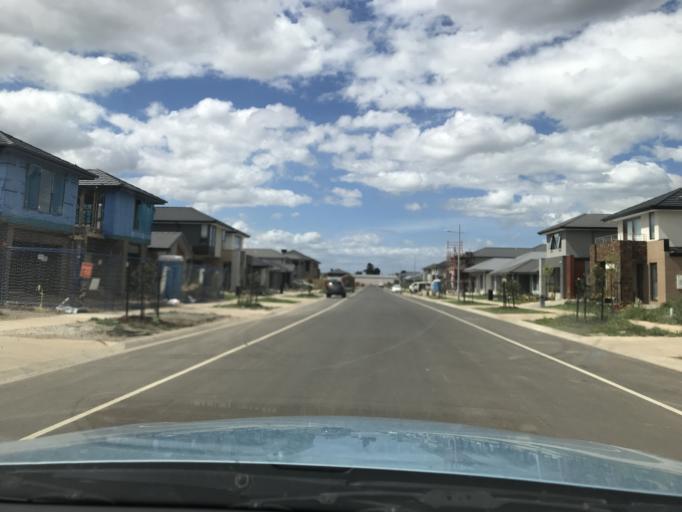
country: AU
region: Victoria
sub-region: Wyndham
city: Williams Landing
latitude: -37.8657
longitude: 144.7539
